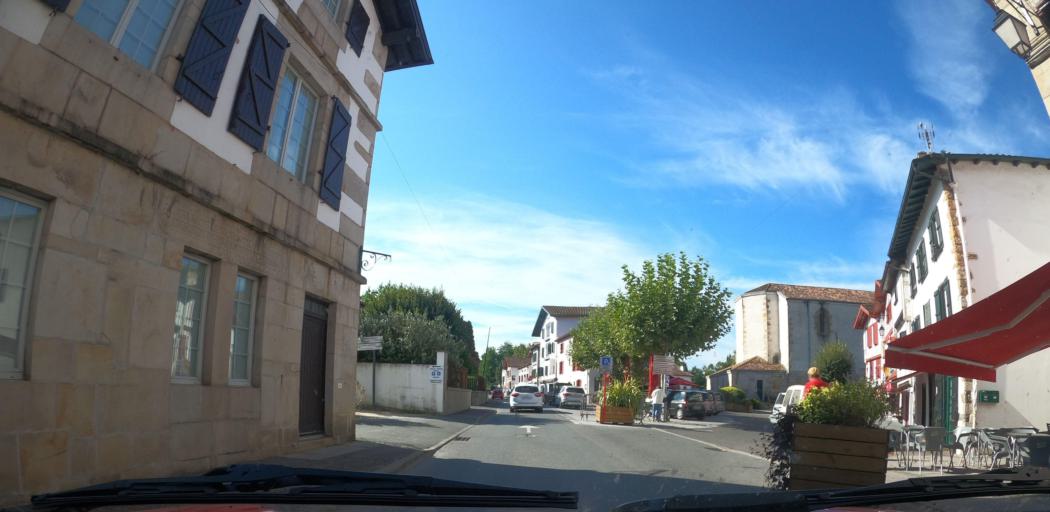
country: FR
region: Aquitaine
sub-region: Departement des Pyrenees-Atlantiques
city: Saint-Pee-sur-Nivelle
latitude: 43.3555
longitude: -1.5505
